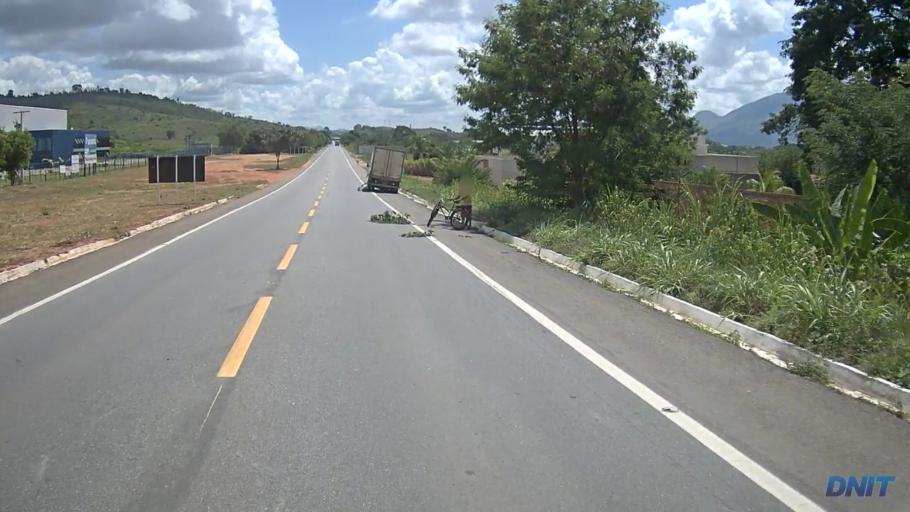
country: BR
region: Minas Gerais
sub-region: Governador Valadares
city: Governador Valadares
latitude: -18.9221
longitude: -42.0168
